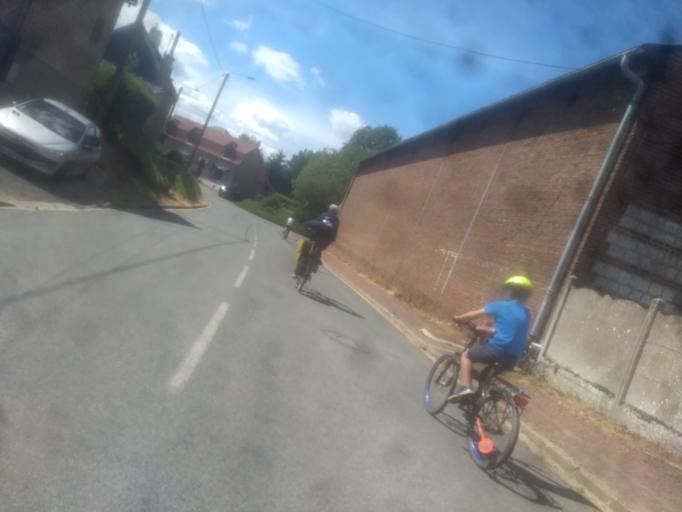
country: FR
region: Nord-Pas-de-Calais
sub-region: Departement du Pas-de-Calais
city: Tilloy-les-Mofflaines
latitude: 50.2488
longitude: 2.8254
